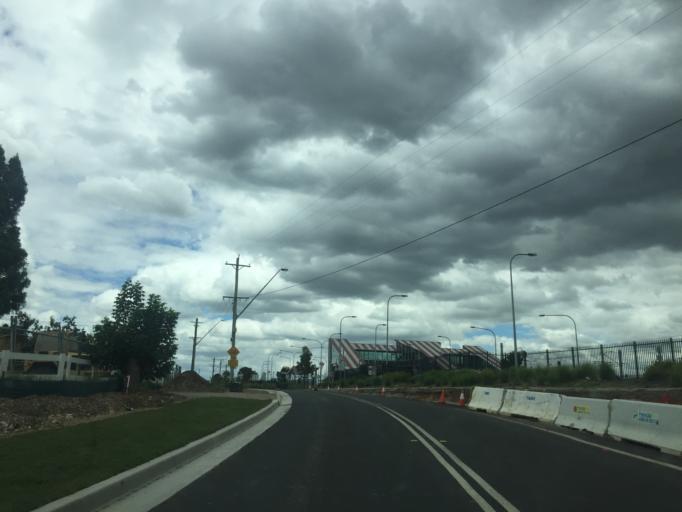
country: AU
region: New South Wales
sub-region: Blacktown
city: Riverstone
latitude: -33.7030
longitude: 150.8738
